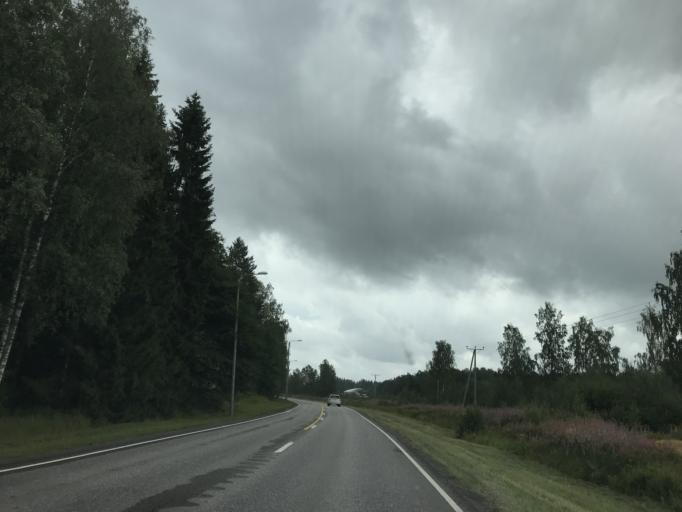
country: FI
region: Uusimaa
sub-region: Raaseporin
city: Ekenaes
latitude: 60.0013
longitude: 23.4027
